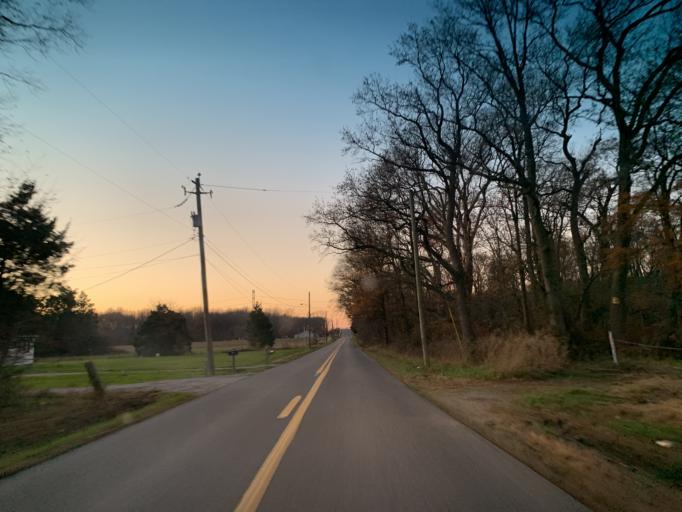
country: US
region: Delaware
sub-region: New Castle County
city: Middletown
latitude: 39.4132
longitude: -75.7599
